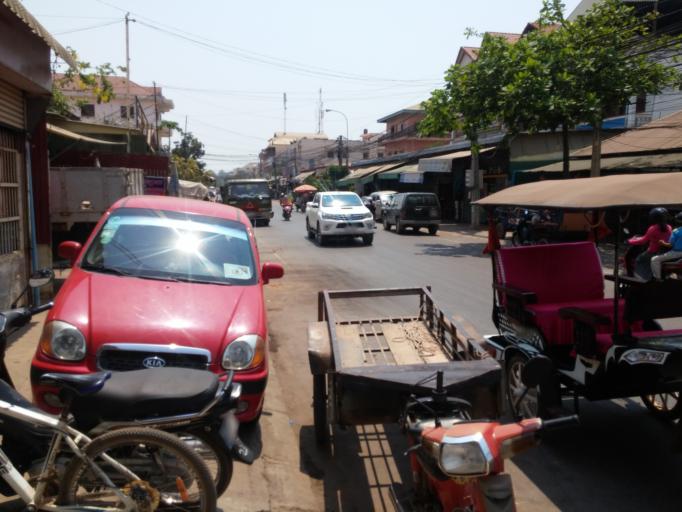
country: KH
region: Siem Reap
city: Siem Reap
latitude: 13.3586
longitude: 103.8609
